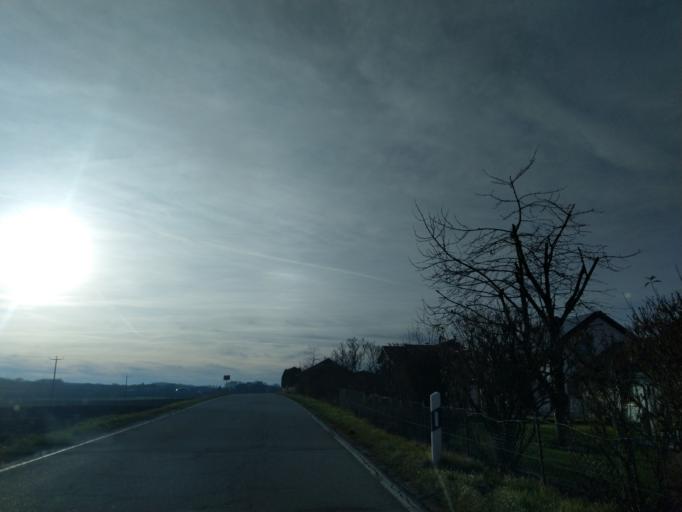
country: DE
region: Bavaria
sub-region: Lower Bavaria
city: Oberporing
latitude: 48.7011
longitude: 12.8198
